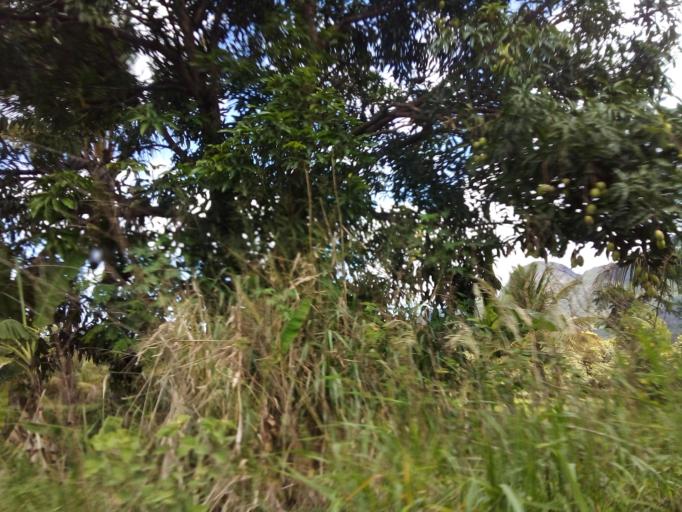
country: BR
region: Espirito Santo
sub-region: Ibiracu
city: Ibiracu
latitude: -19.8800
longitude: -40.3627
